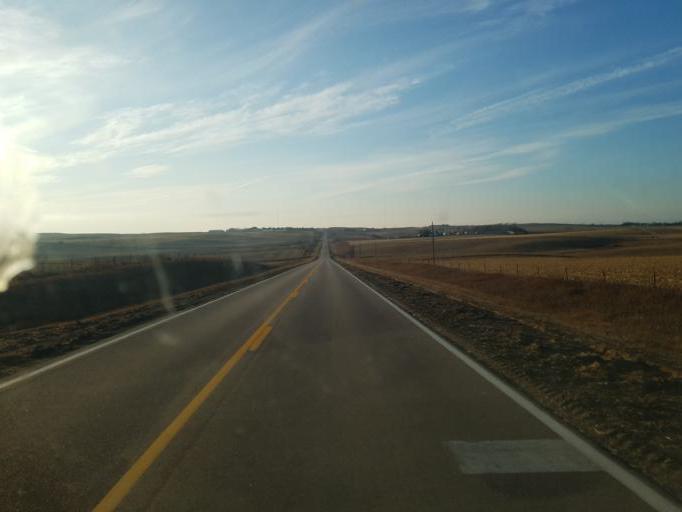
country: US
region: South Dakota
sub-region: Yankton County
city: Yankton
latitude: 42.7287
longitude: -97.3772
